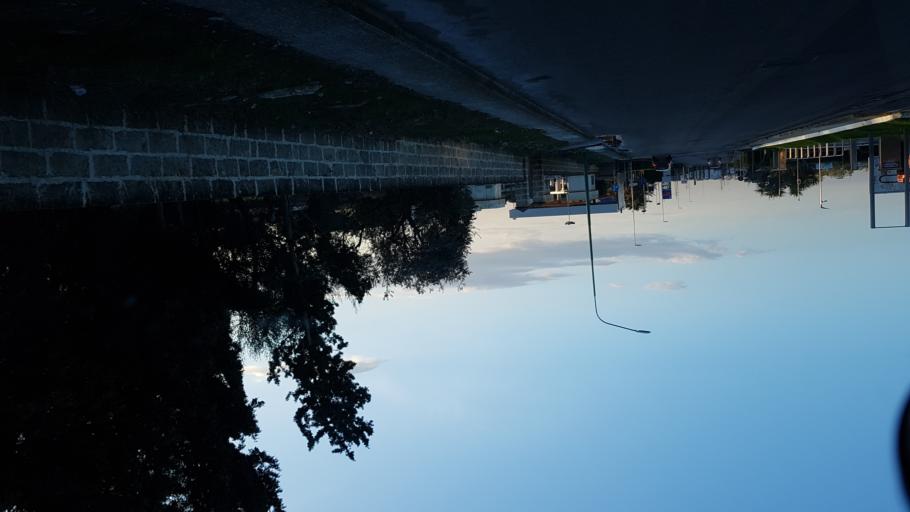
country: IT
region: Apulia
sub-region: Provincia di Lecce
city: Giorgilorio
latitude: 40.3771
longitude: 18.1412
